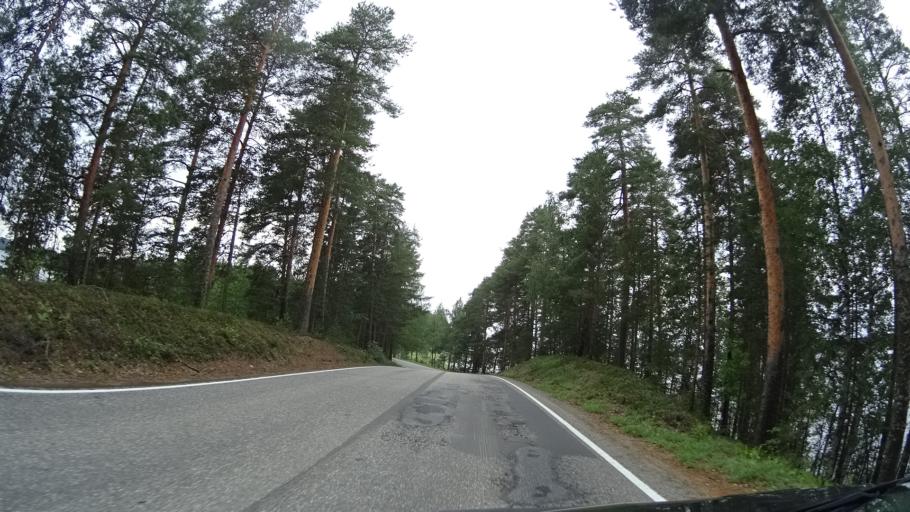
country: FI
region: Southern Savonia
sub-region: Savonlinna
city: Punkaharju
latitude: 61.7546
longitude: 29.4241
